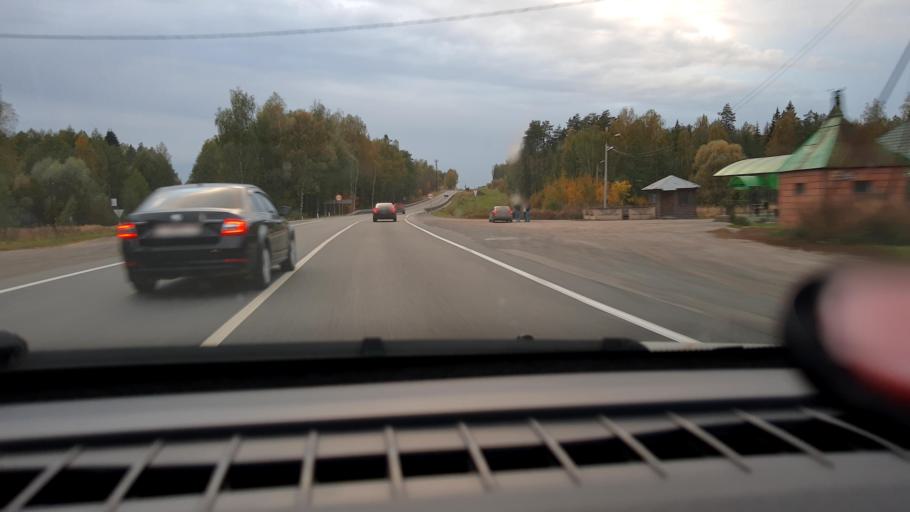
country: RU
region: Vladimir
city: Kameshkovo
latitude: 56.1933
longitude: 40.9294
